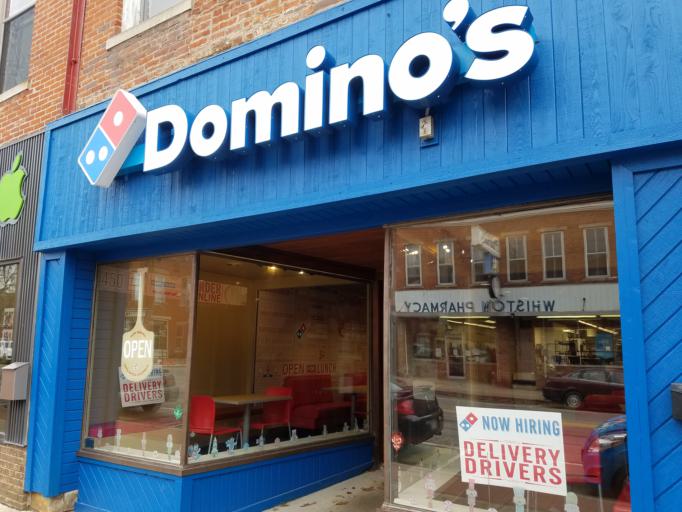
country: US
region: Ohio
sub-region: Morrow County
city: Mount Gilead
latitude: 40.5426
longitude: -82.8265
